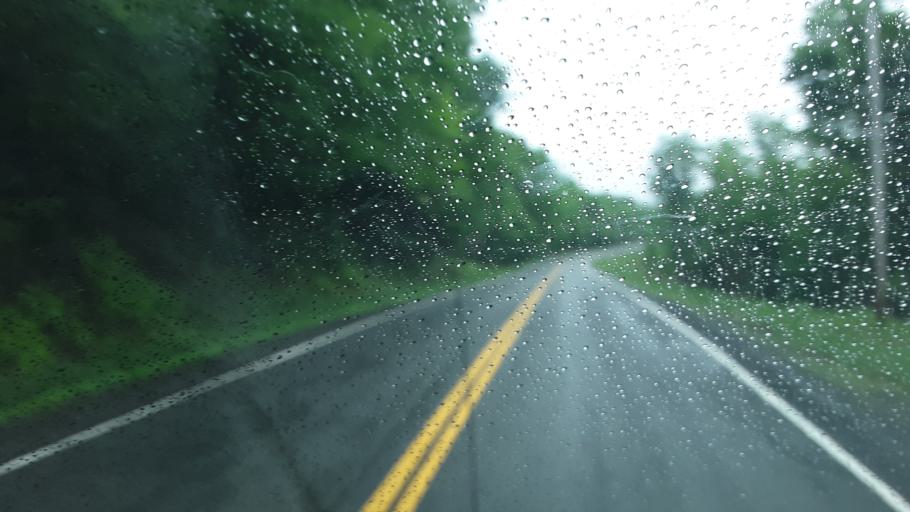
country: US
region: Maine
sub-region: Penobscot County
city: Patten
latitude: 46.1583
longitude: -68.3497
